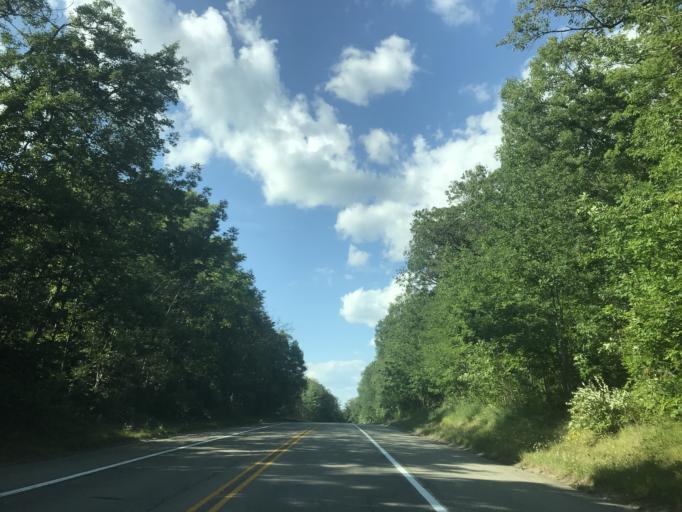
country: US
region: Michigan
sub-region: Newaygo County
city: Newaygo
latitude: 43.4463
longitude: -85.7814
